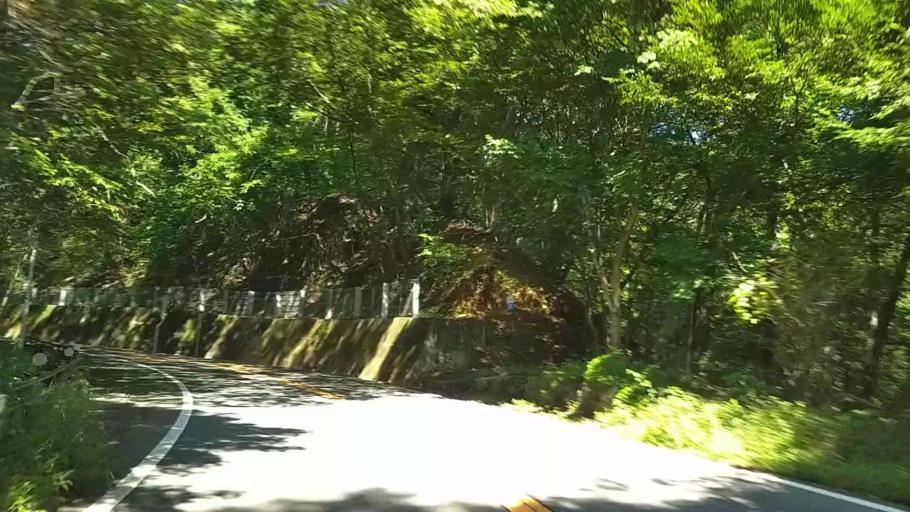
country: JP
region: Nagano
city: Saku
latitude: 36.3547
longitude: 138.6635
